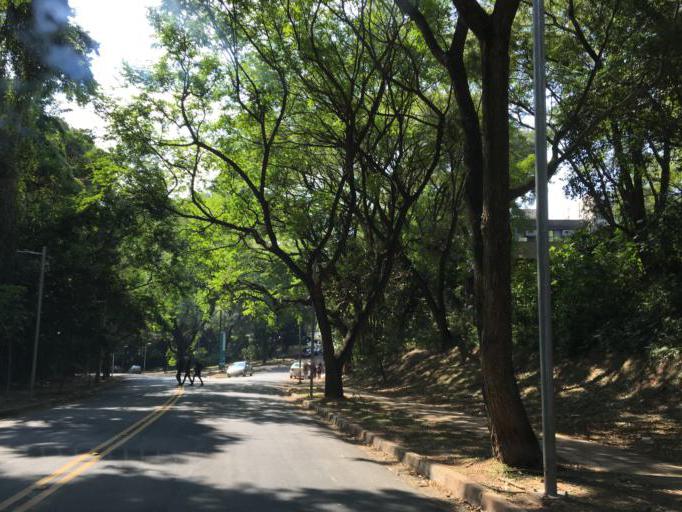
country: BR
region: Sao Paulo
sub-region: Osasco
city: Osasco
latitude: -23.5656
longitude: -46.7273
